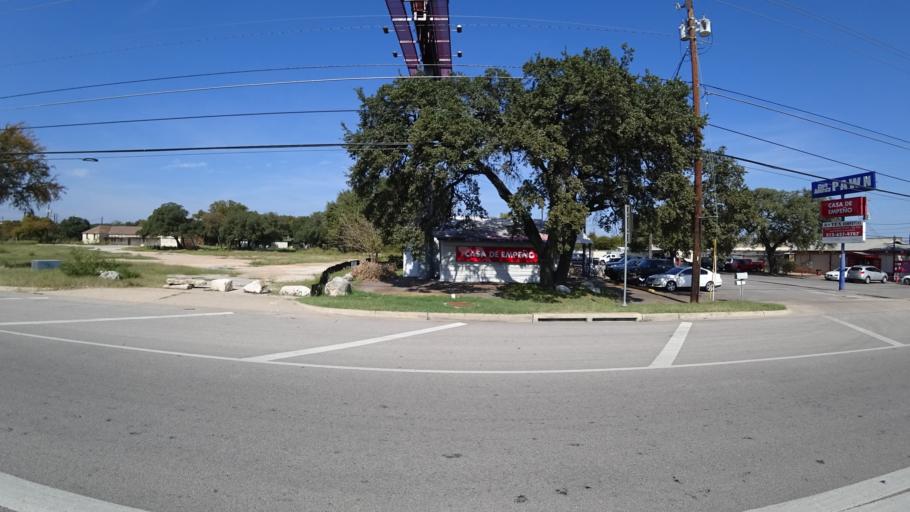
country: US
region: Texas
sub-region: Travis County
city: Barton Creek
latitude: 30.2355
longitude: -97.8570
